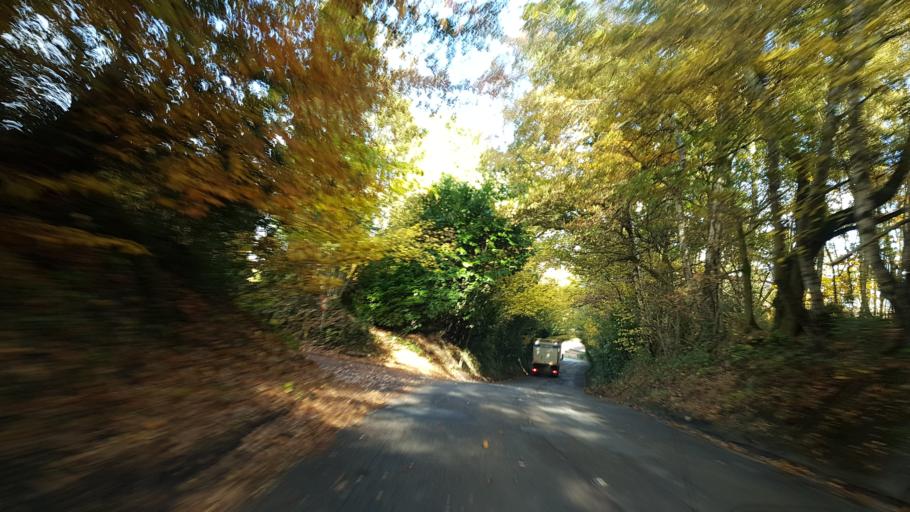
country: GB
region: England
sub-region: Surrey
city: Churt
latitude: 51.1345
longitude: -0.7514
